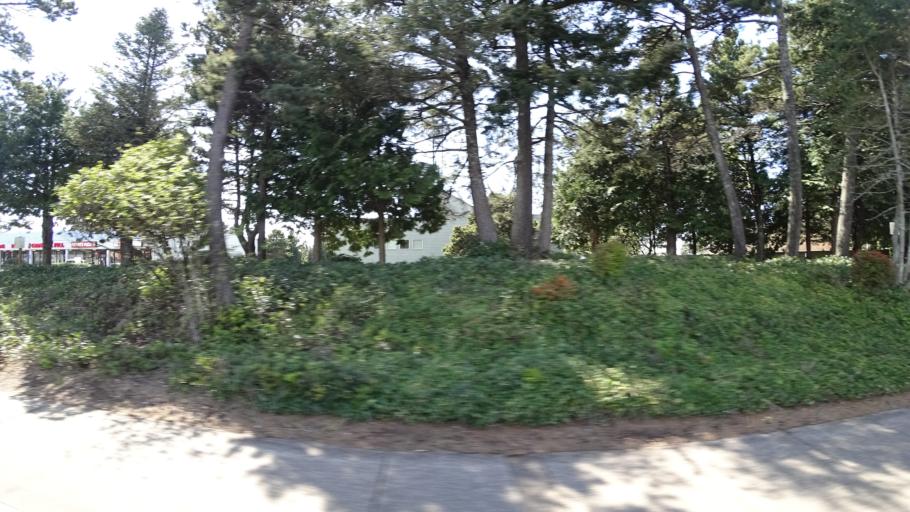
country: US
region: Oregon
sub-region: Lincoln County
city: Newport
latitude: 44.6525
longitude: -124.0531
